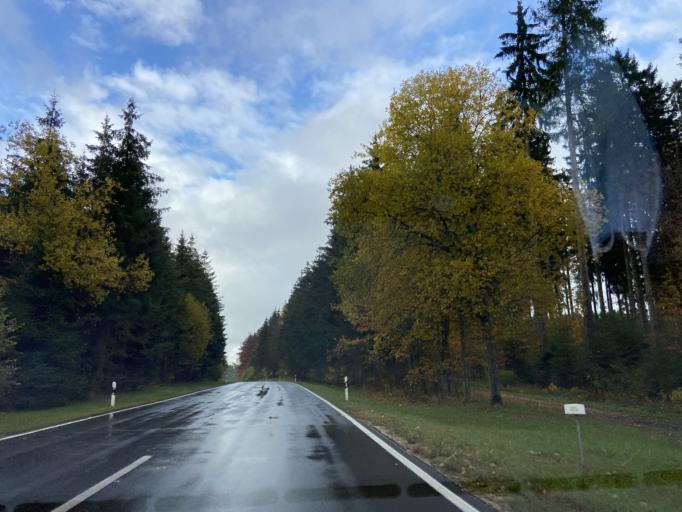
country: DE
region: Baden-Wuerttemberg
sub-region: Freiburg Region
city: Irndorf
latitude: 48.0917
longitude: 8.9622
